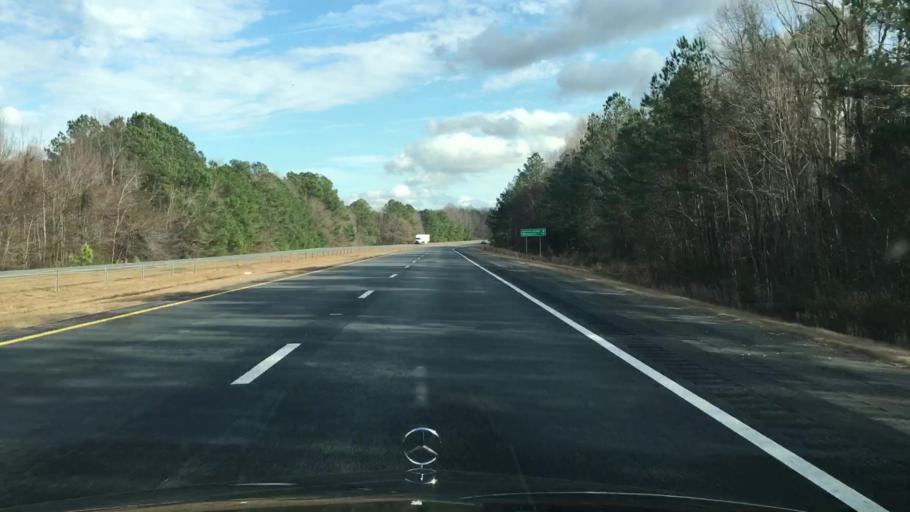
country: US
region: North Carolina
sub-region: Johnston County
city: Four Oaks
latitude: 35.3268
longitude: -78.4357
